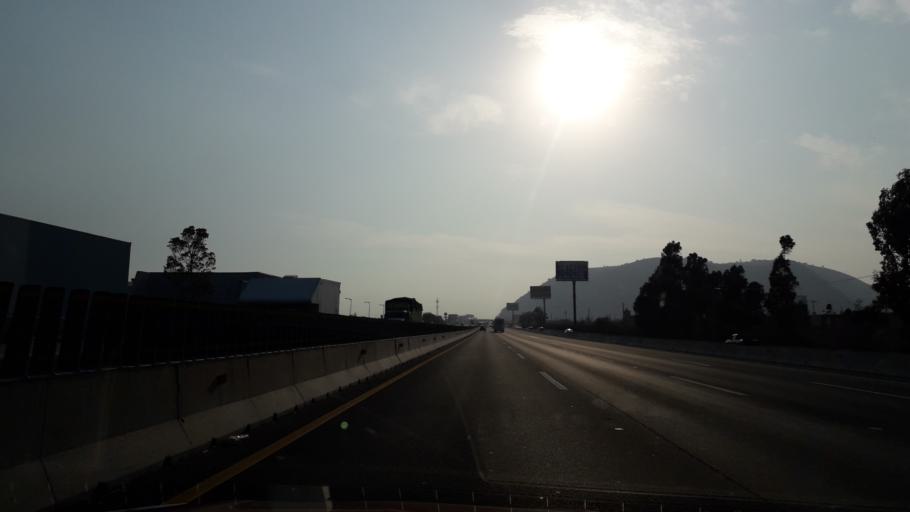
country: MX
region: Mexico
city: Ixtapaluca
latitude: 19.2924
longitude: -98.8927
